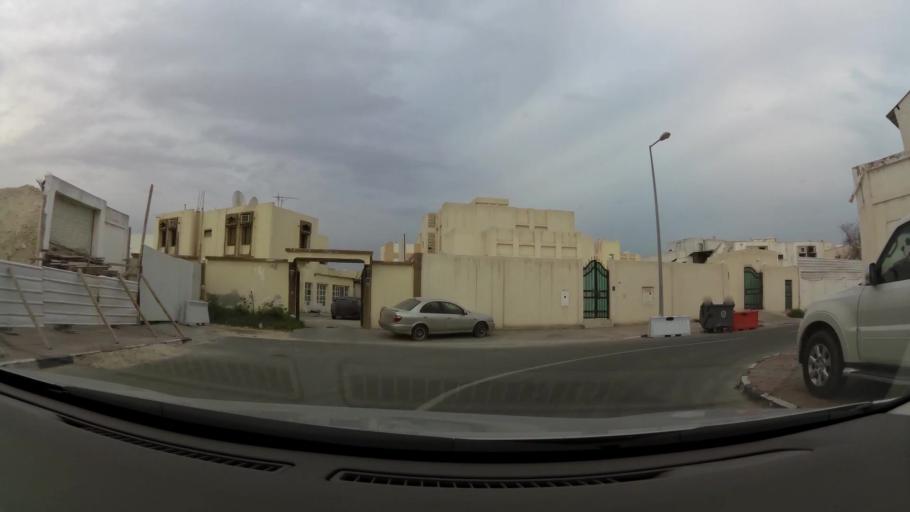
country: QA
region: Baladiyat ad Dawhah
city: Doha
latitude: 25.3384
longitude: 51.5075
